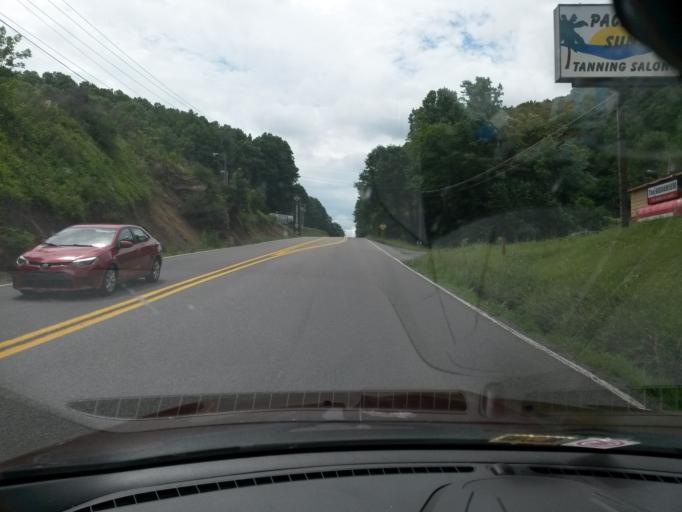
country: US
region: West Virginia
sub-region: Mercer County
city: Brush Fork
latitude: 37.2717
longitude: -81.2448
